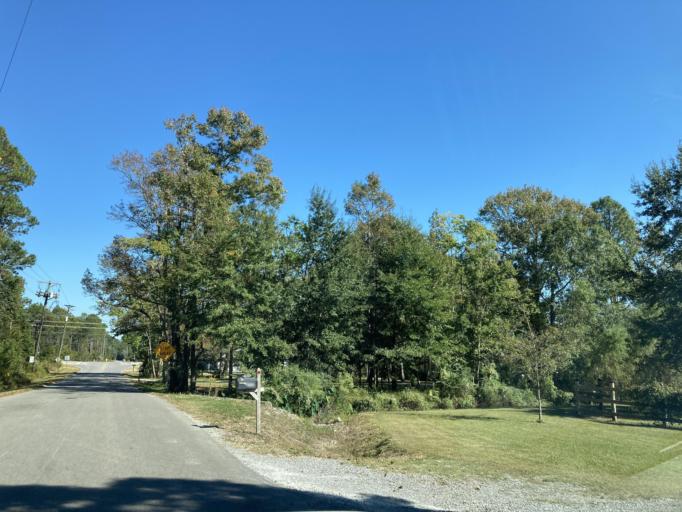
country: US
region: Mississippi
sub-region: Jackson County
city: Saint Martin
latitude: 30.4649
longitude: -88.8485
